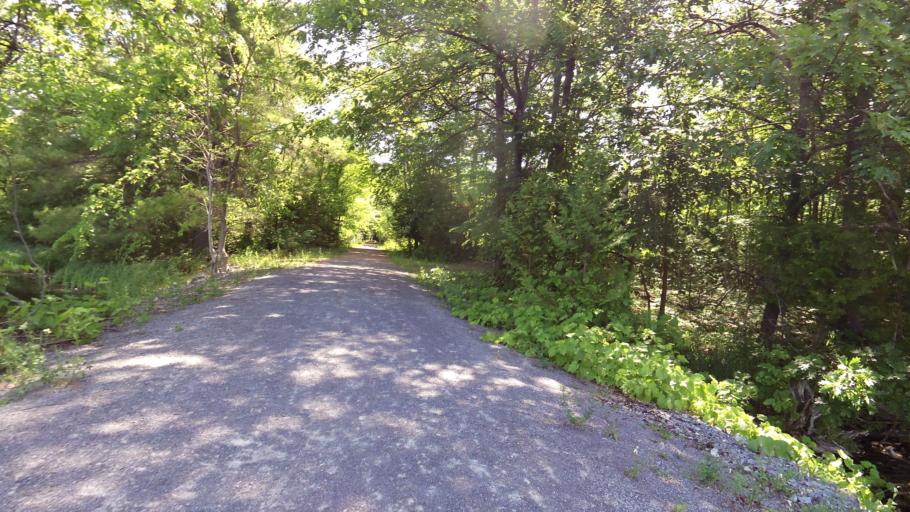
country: CA
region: Ontario
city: Arnprior
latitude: 45.4595
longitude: -76.2626
